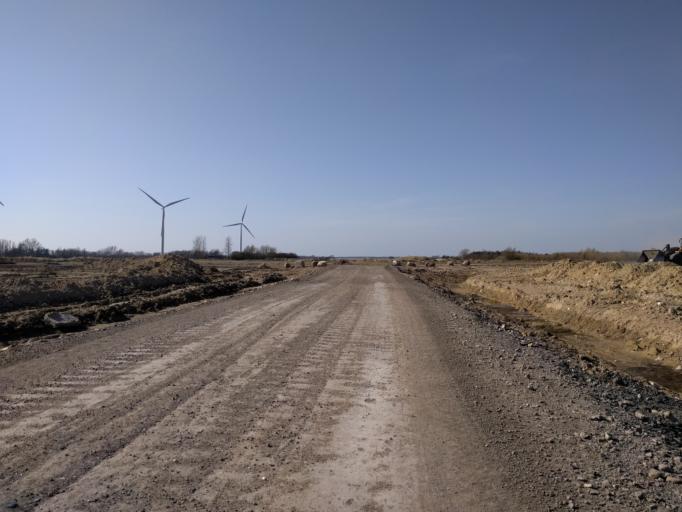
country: DK
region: South Denmark
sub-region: Kerteminde Kommune
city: Munkebo
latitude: 55.4593
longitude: 10.5222
